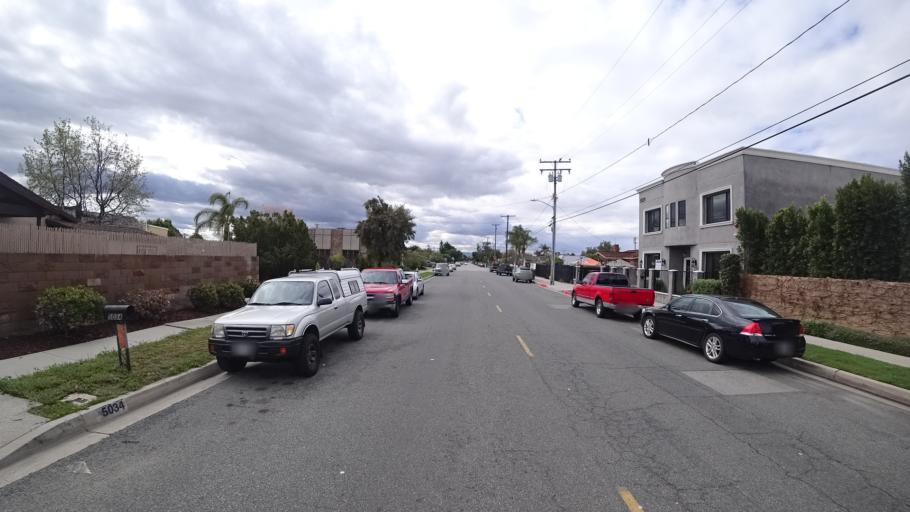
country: US
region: California
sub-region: Los Angeles County
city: Irwindale
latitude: 34.1044
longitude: -117.9551
